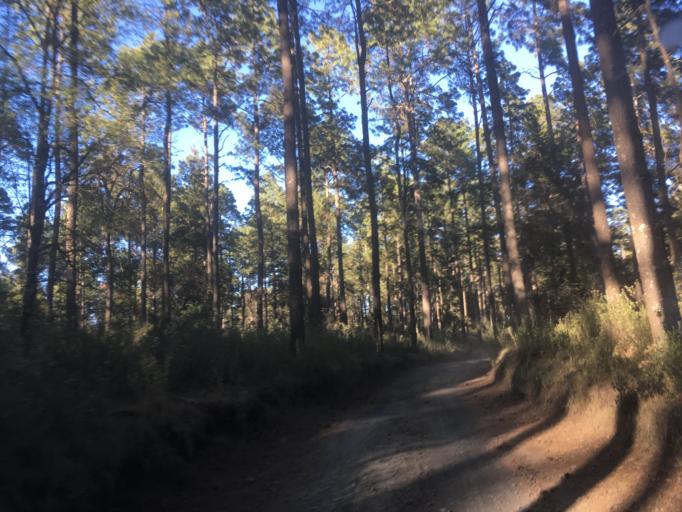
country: MX
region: Michoacan
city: Angahuan
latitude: 19.4630
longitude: -102.2223
